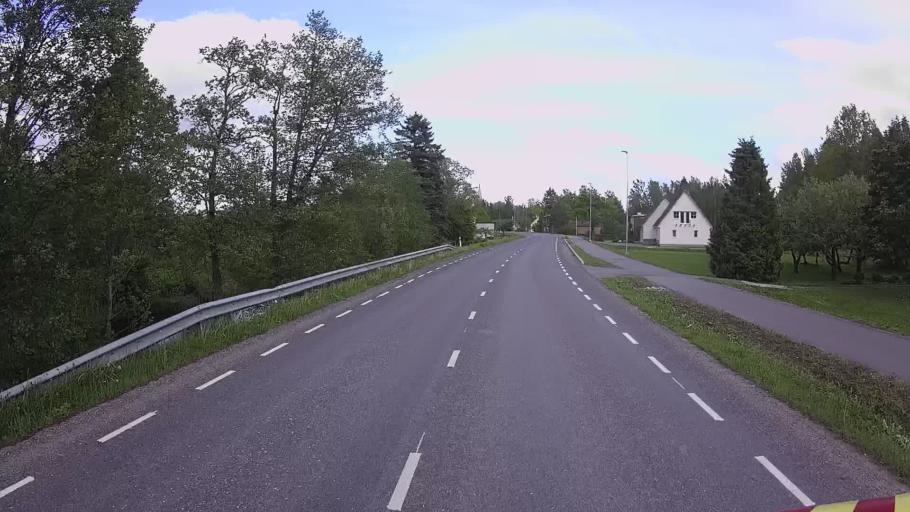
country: EE
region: Jogevamaa
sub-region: Mustvee linn
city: Mustvee
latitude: 58.9865
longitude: 26.8569
